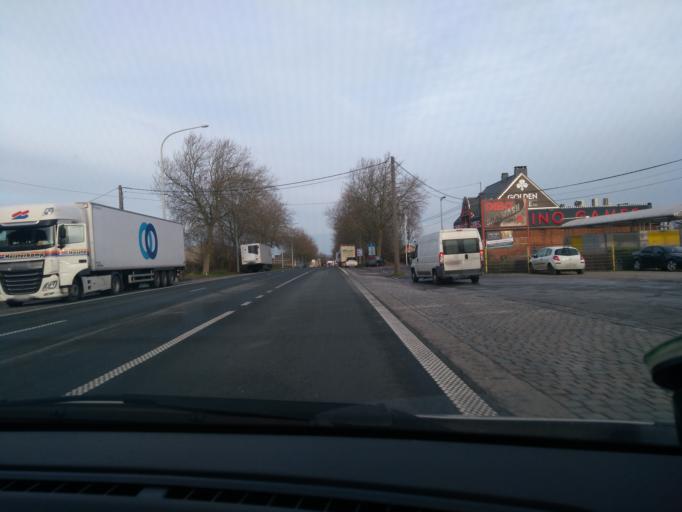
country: BE
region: Wallonia
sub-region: Province du Hainaut
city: Quevy-le-Petit
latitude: 50.3455
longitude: 3.9699
